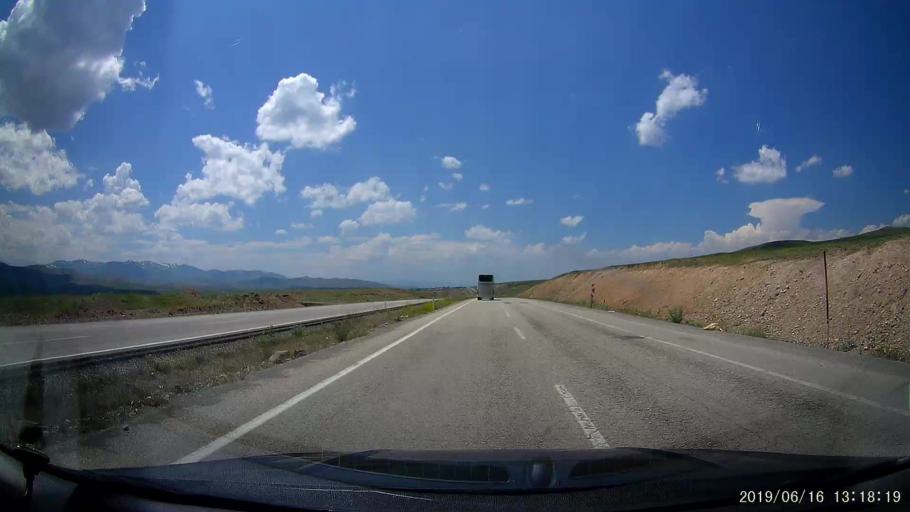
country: TR
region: Agri
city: Taslicay
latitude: 39.6303
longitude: 43.4330
